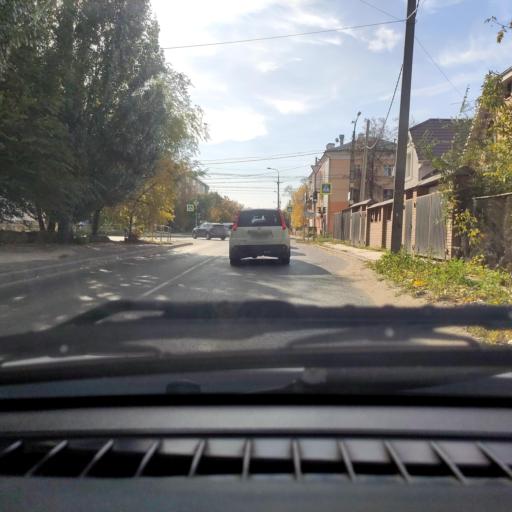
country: RU
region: Samara
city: Tol'yatti
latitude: 53.5069
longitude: 49.3993
